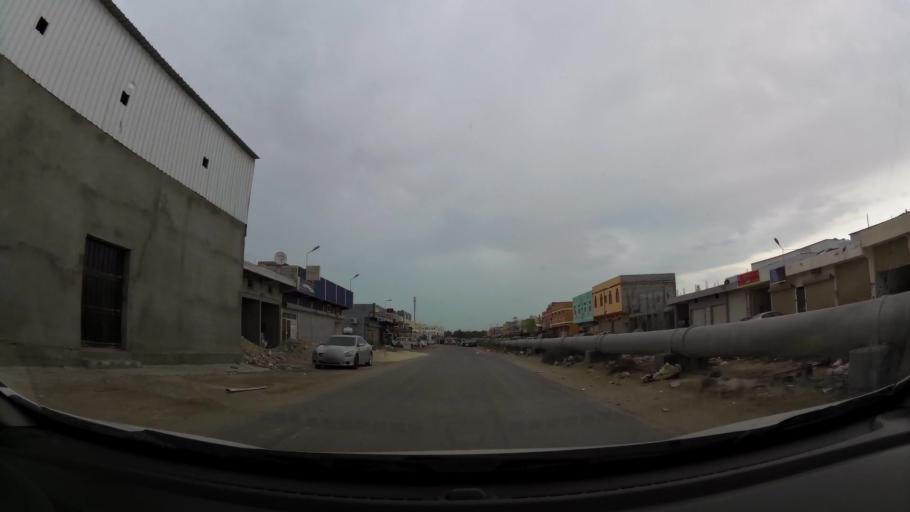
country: BH
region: Central Governorate
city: Madinat Hamad
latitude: 26.1443
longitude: 50.4862
